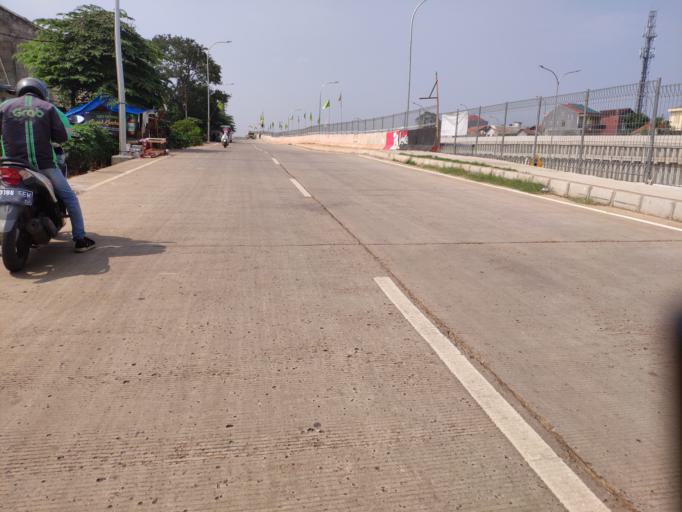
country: ID
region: West Java
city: Pamulang
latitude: -6.3298
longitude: 106.8008
